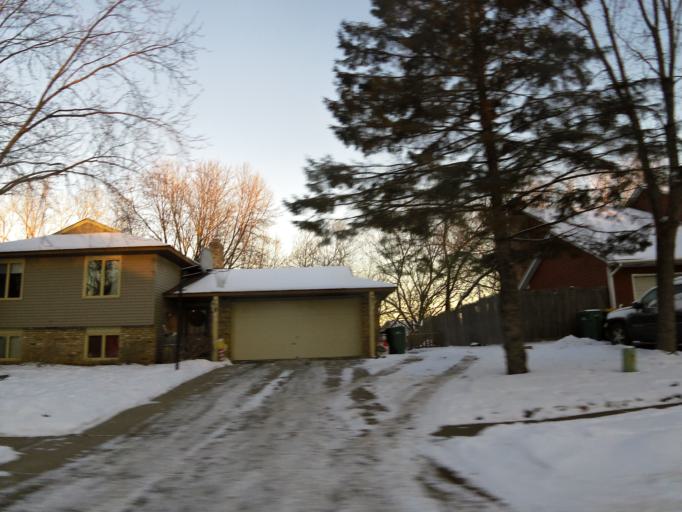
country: US
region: Minnesota
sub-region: Washington County
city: Stillwater
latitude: 45.0565
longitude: -92.8389
